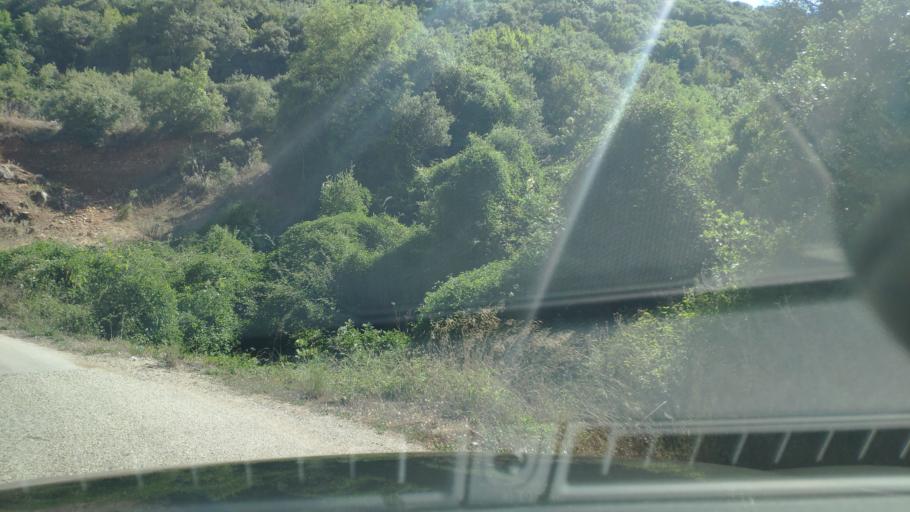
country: GR
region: West Greece
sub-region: Nomos Aitolias kai Akarnanias
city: Katouna
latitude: 38.8078
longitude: 21.1067
